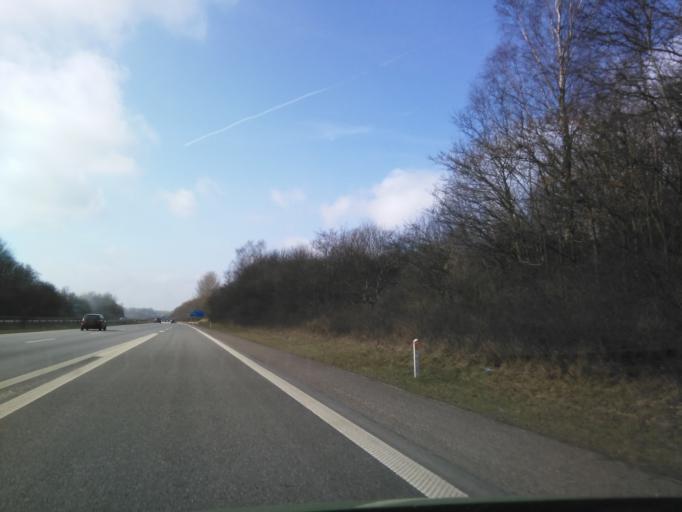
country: DK
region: Central Jutland
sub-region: Skanderborg Kommune
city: Skanderborg
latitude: 56.0489
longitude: 9.9193
